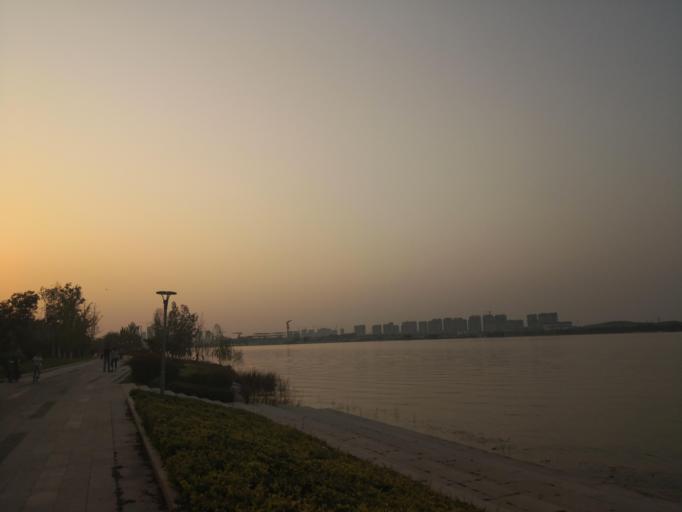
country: CN
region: Henan Sheng
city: Zhongyuanlu
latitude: 35.8006
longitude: 115.0462
